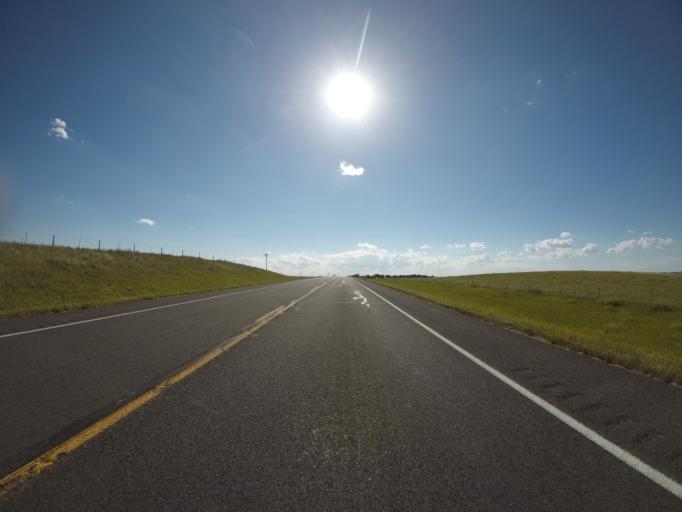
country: US
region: Colorado
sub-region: Morgan County
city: Brush
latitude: 40.6107
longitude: -103.5925
